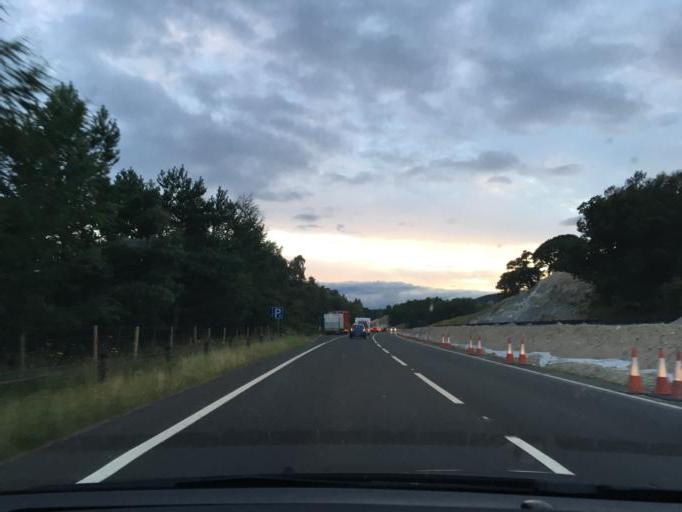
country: GB
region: Scotland
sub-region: Highland
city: Kingussie
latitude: 57.1140
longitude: -3.9522
